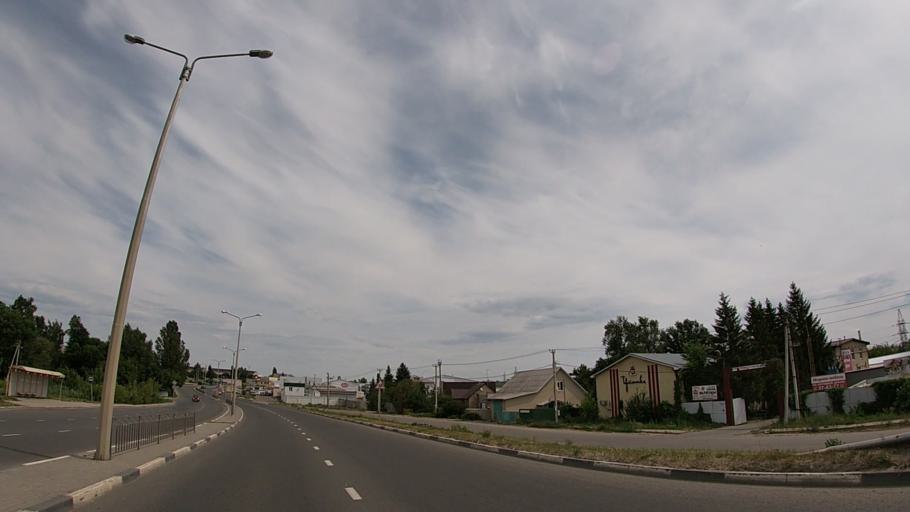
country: RU
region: Belgorod
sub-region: Belgorodskiy Rayon
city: Belgorod
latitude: 50.6089
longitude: 36.5336
